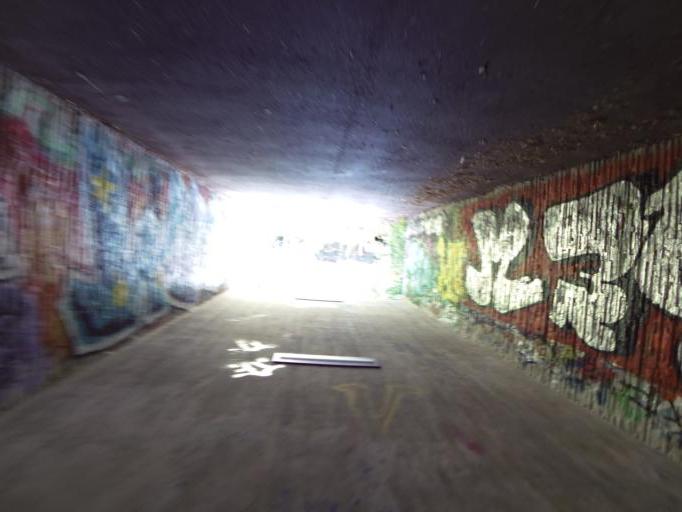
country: DK
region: Capital Region
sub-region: Frederiksberg Kommune
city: Frederiksberg
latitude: 55.7265
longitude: 12.5386
